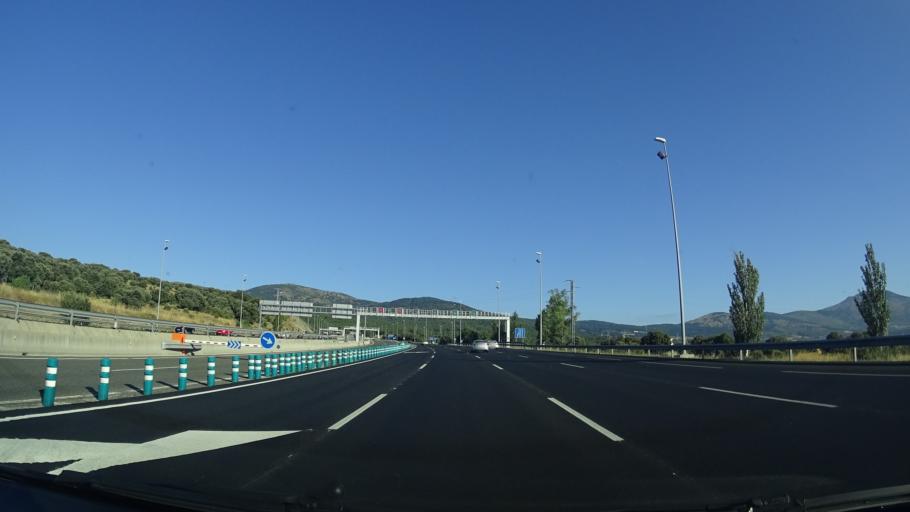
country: ES
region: Madrid
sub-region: Provincia de Madrid
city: Guadarrama
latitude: 40.6676
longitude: -4.1029
